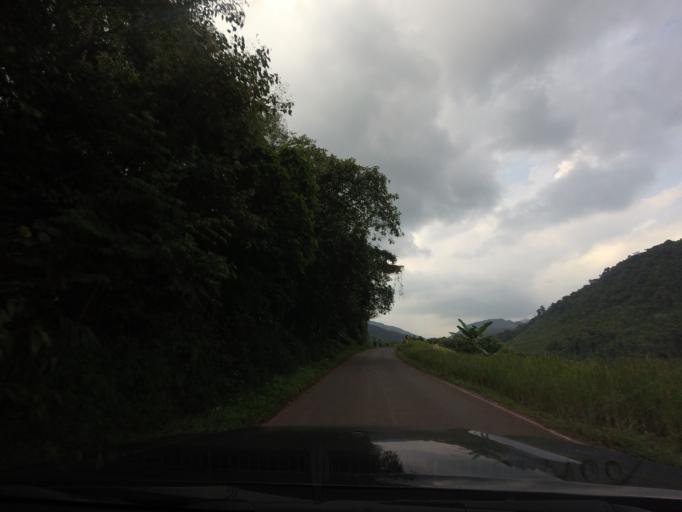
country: TH
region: Nan
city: Bo Kluea
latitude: 19.2737
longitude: 101.1776
